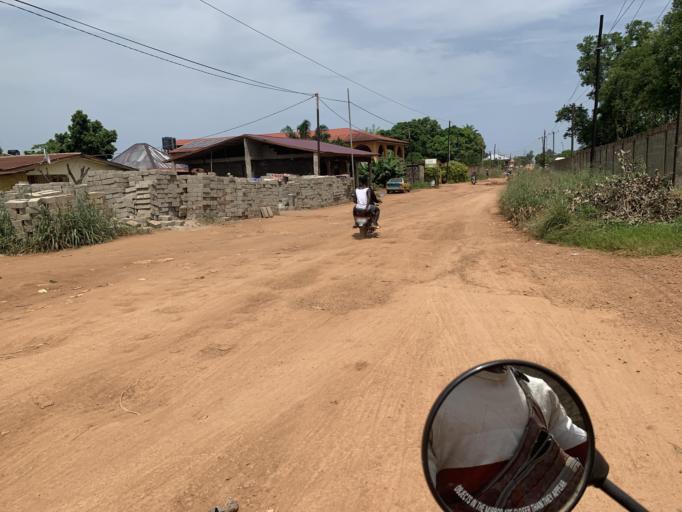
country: SL
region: Western Area
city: Hastings
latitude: 8.4025
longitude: -13.1372
